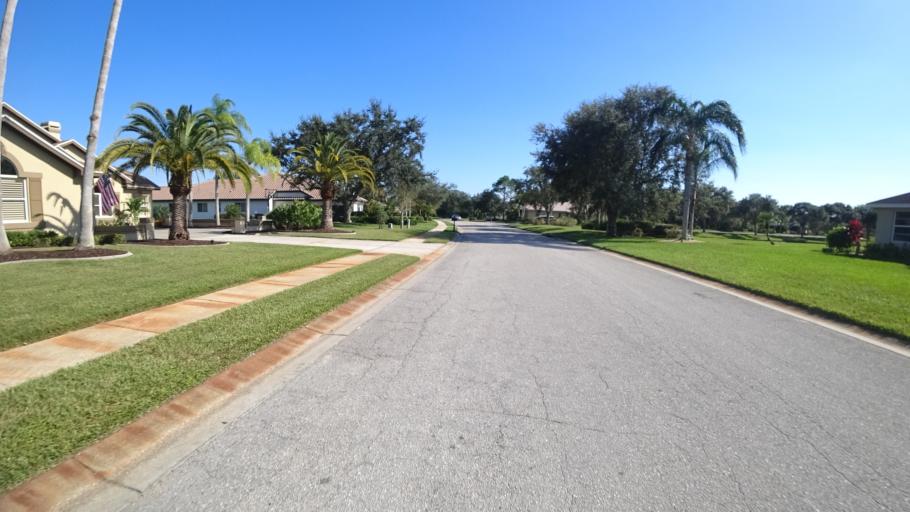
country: US
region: Florida
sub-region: Sarasota County
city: The Meadows
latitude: 27.4063
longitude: -82.4416
